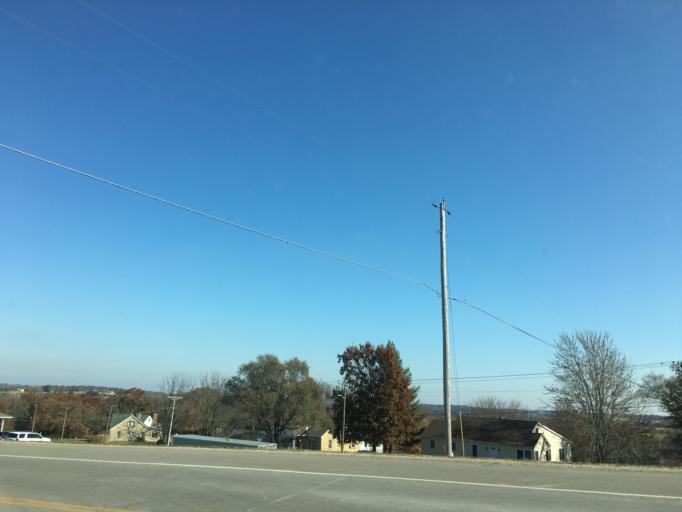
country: US
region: Missouri
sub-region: Cole County
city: Wardsville
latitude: 38.4975
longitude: -92.1779
